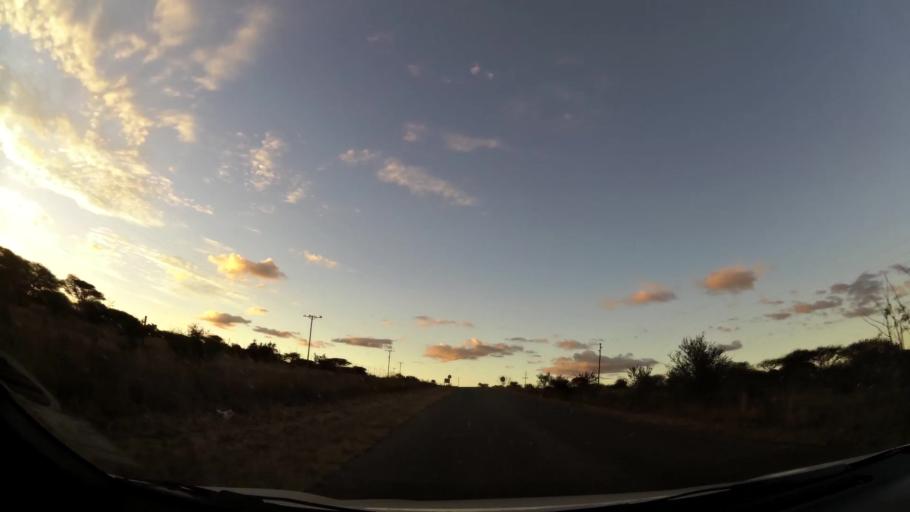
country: ZA
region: Limpopo
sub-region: Capricorn District Municipality
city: Polokwane
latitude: -23.7662
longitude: 29.4745
